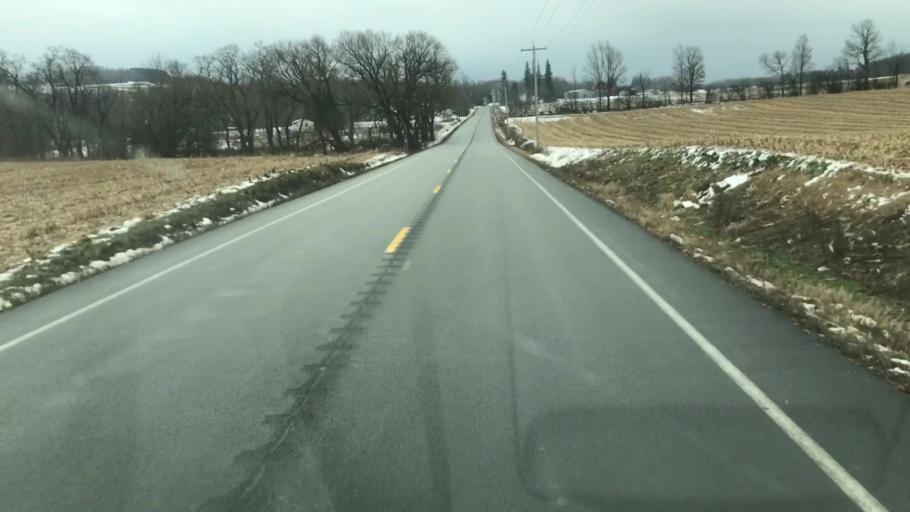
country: US
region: New York
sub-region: Cayuga County
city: Moravia
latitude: 42.8145
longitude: -76.3486
